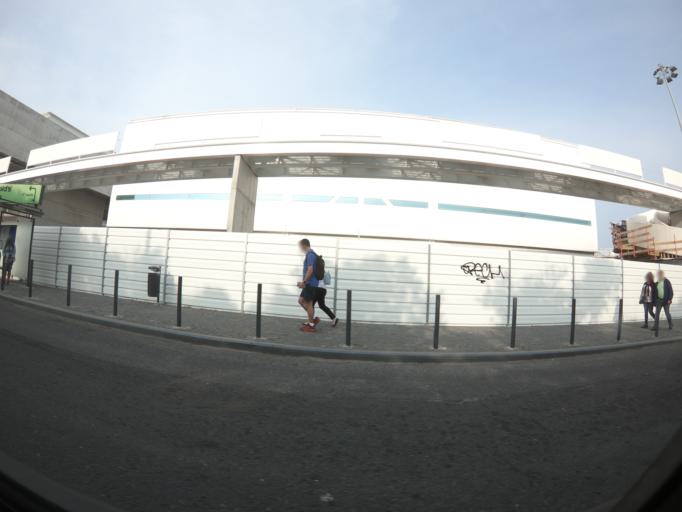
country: PT
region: Setubal
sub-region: Almada
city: Caparica
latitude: 38.6966
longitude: -9.1991
